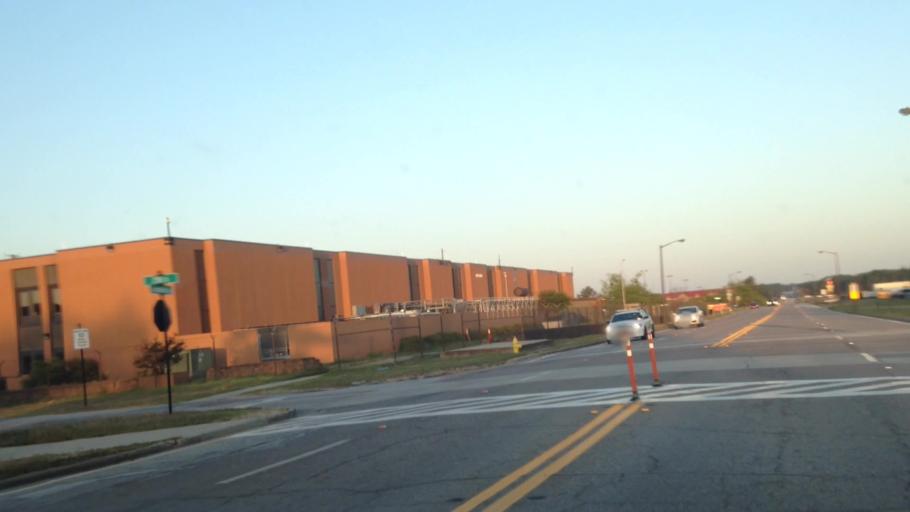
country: US
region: Georgia
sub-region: Columbia County
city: Grovetown
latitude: 33.4255
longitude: -82.1521
